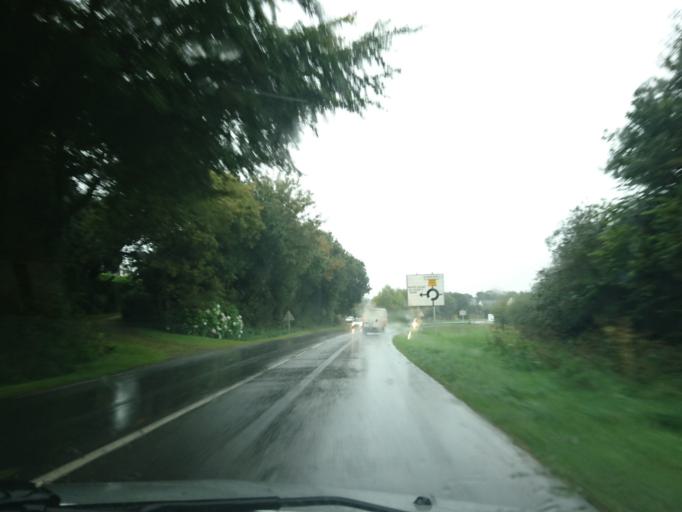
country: FR
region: Brittany
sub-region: Departement du Finistere
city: Plabennec
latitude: 48.4911
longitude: -4.4337
